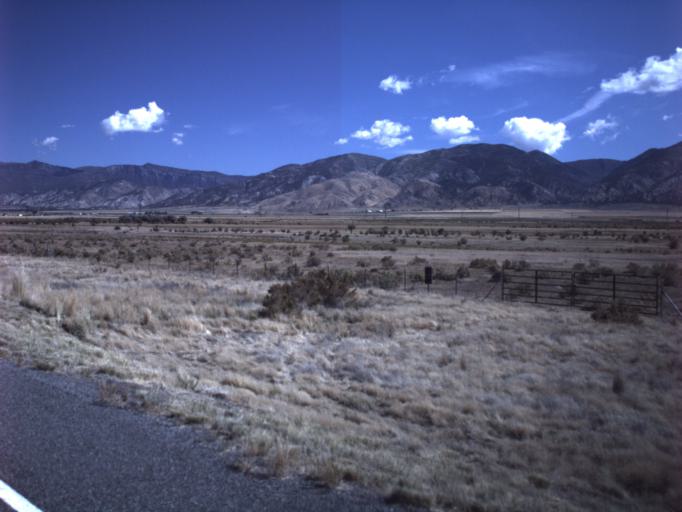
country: US
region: Utah
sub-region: Juab County
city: Nephi
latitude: 39.5067
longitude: -111.9519
